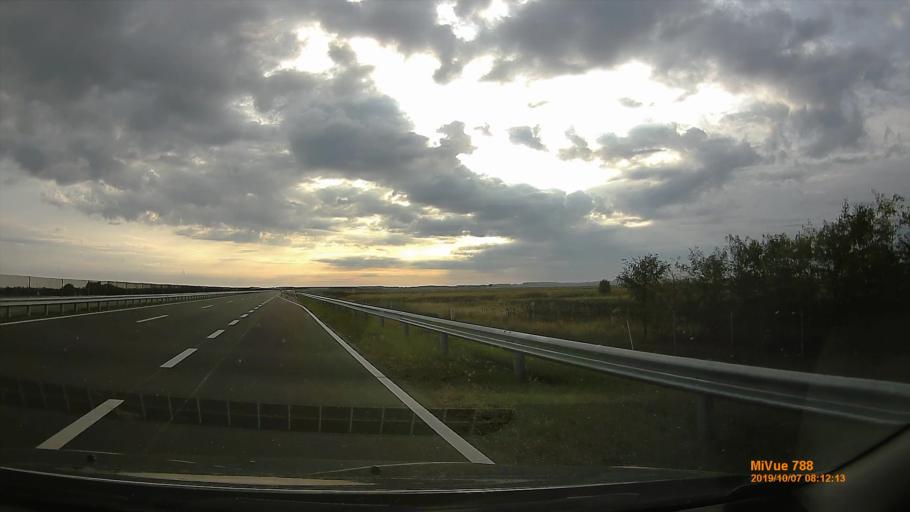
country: HU
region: Jasz-Nagykun-Szolnok
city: Cserkeszolo
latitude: 46.8836
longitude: 20.2213
